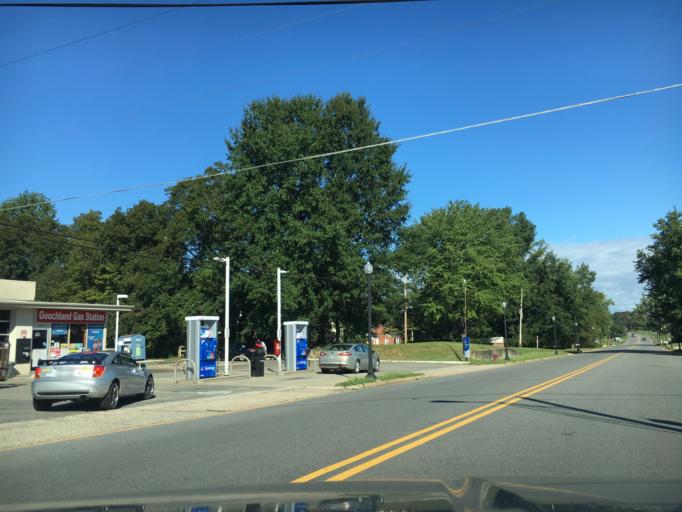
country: US
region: Virginia
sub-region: Goochland County
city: Goochland
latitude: 37.6842
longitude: -77.8853
